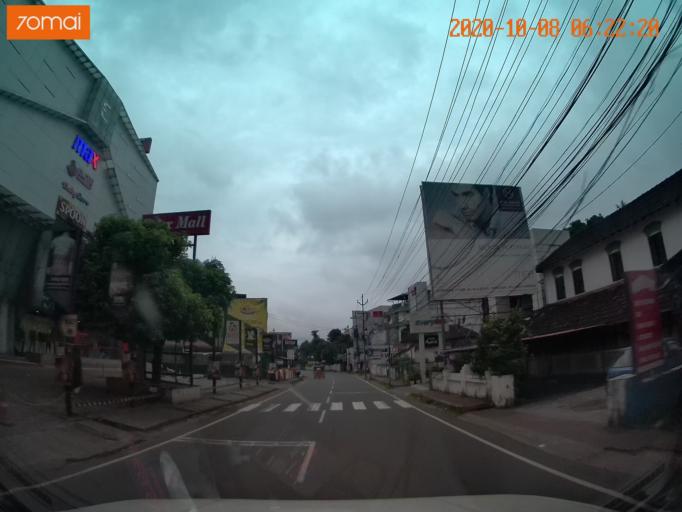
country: IN
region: Kerala
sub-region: Thrissur District
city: Trichur
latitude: 10.5231
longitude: 76.2248
